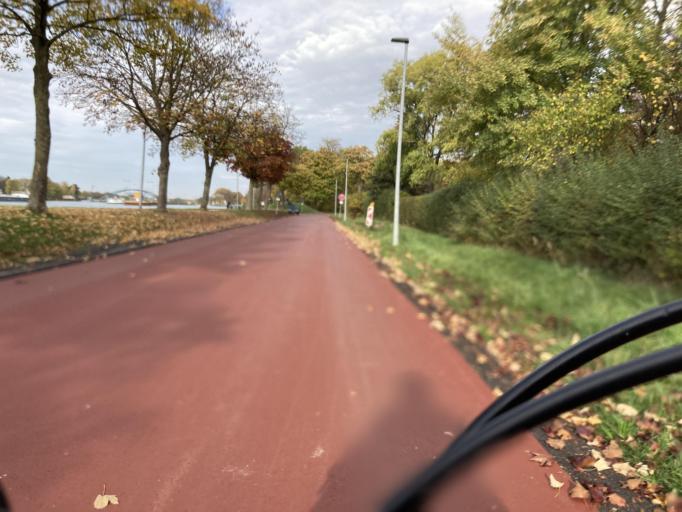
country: DE
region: North Rhine-Westphalia
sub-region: Regierungsbezirk Munster
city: Muenster
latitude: 51.9727
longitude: 7.6640
